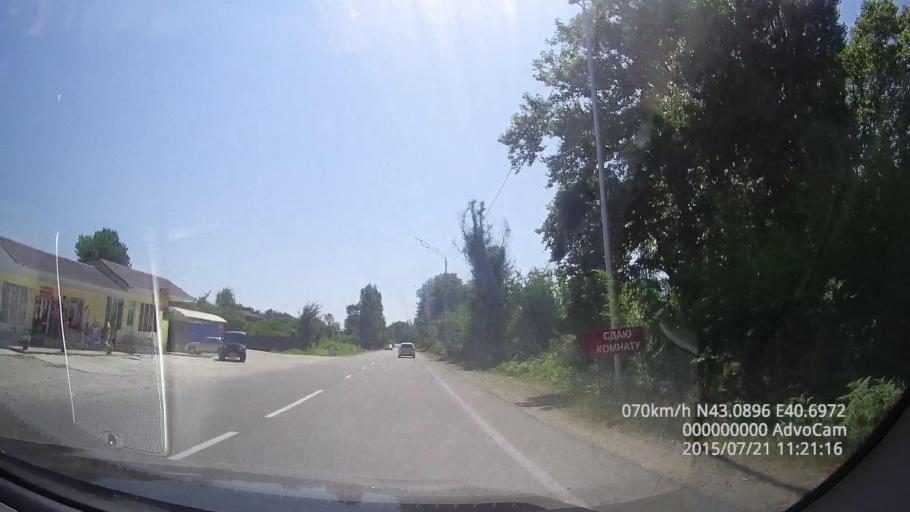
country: GE
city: P'rimorsk'oe
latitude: 43.0895
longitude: 40.6976
